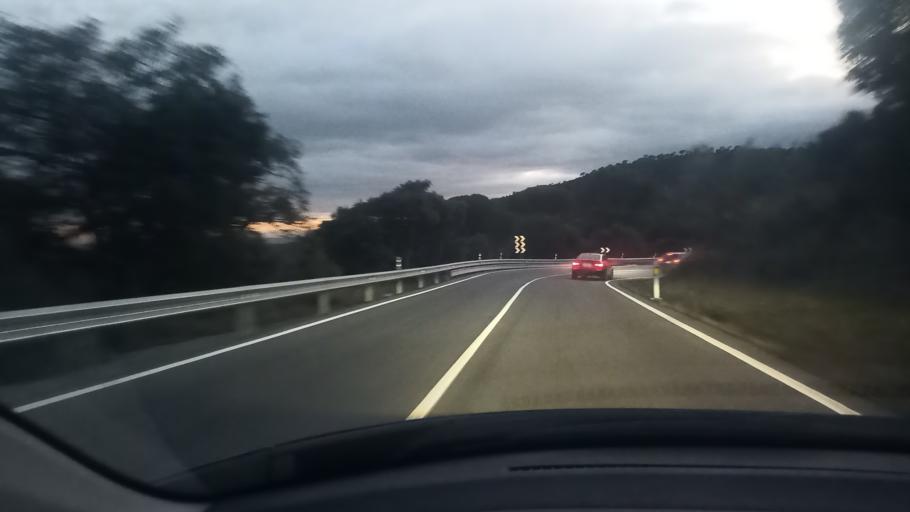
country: ES
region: Madrid
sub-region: Provincia de Madrid
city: Navas del Rey
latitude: 40.4446
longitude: -4.2652
